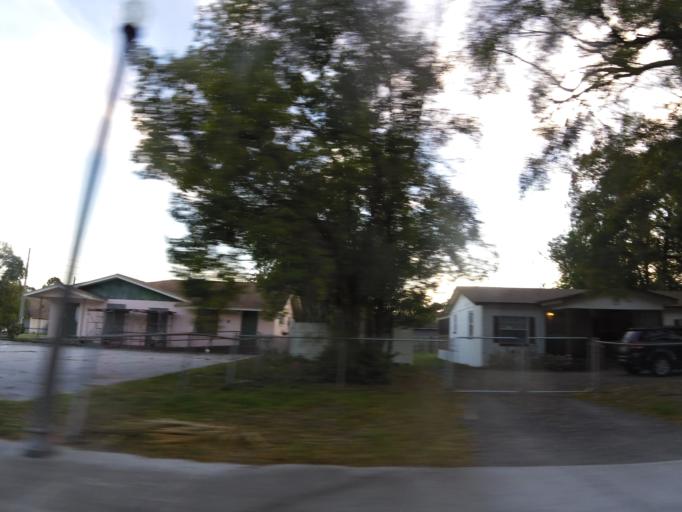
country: US
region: Florida
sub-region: Duval County
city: Jacksonville
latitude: 30.4665
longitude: -81.6287
